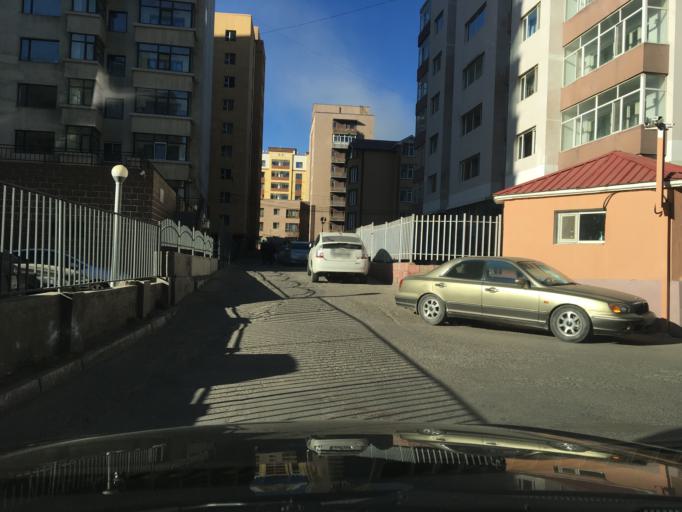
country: MN
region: Ulaanbaatar
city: Ulaanbaatar
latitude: 47.8918
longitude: 106.9007
